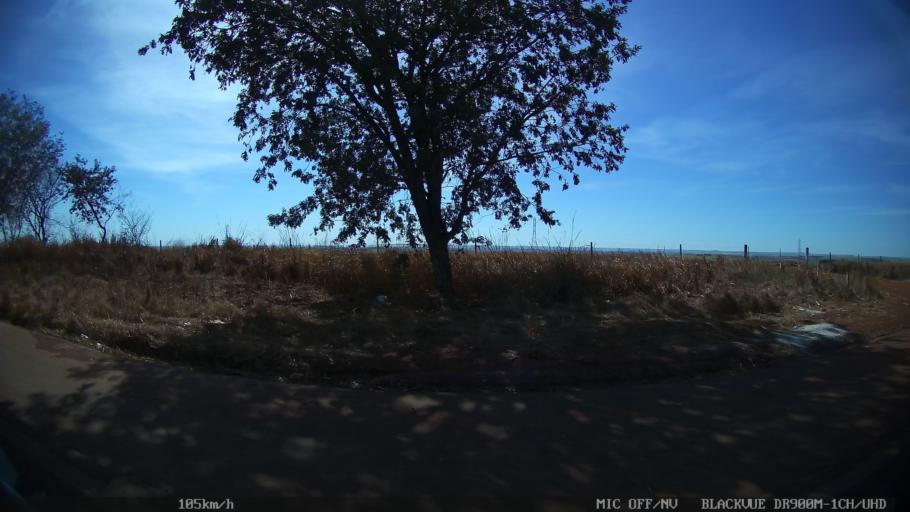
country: BR
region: Sao Paulo
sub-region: Sao Joaquim Da Barra
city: Sao Joaquim da Barra
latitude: -20.5188
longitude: -47.8720
